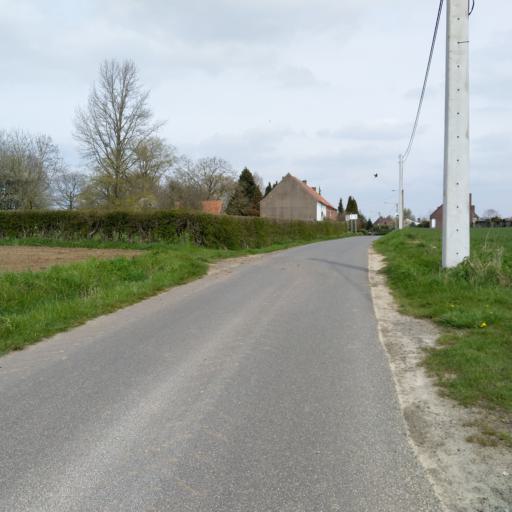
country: FR
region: Nord-Pas-de-Calais
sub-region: Departement du Nord
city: Feignies
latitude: 50.3303
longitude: 3.9013
